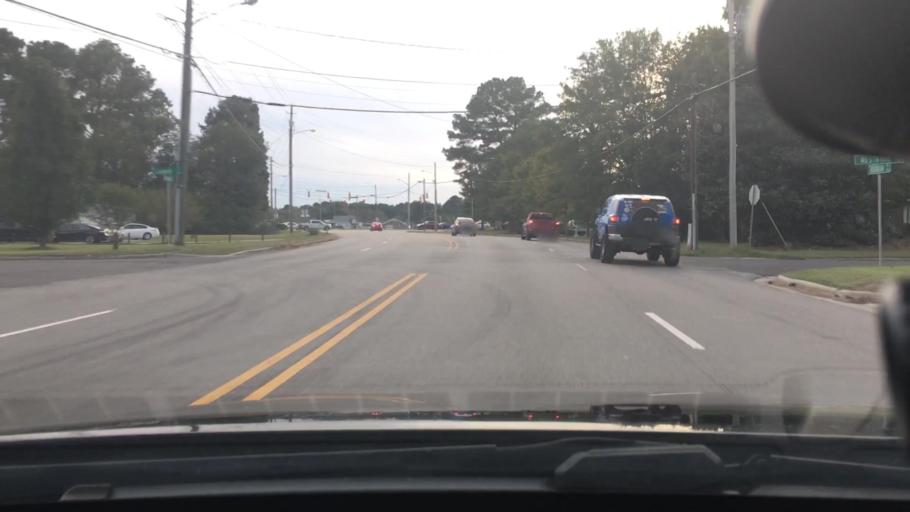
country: US
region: North Carolina
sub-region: Pitt County
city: Summerfield
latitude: 35.5962
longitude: -77.4013
